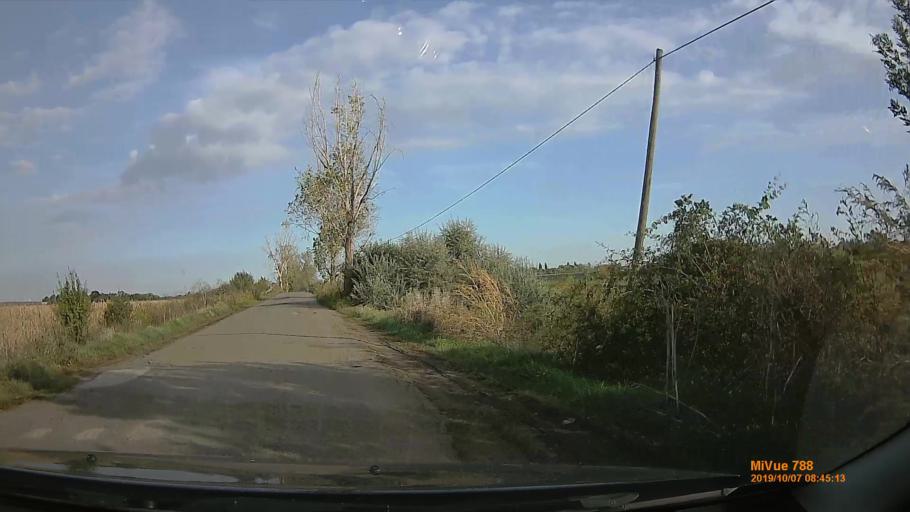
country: HU
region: Bekes
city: Szarvas
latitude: 46.8124
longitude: 20.5268
